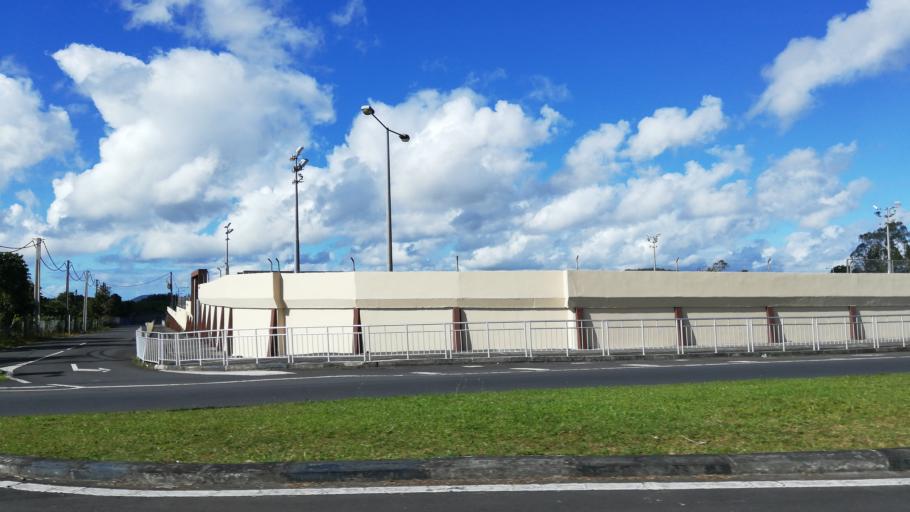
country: MU
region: Moka
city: Providence
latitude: -20.2466
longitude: 57.6033
